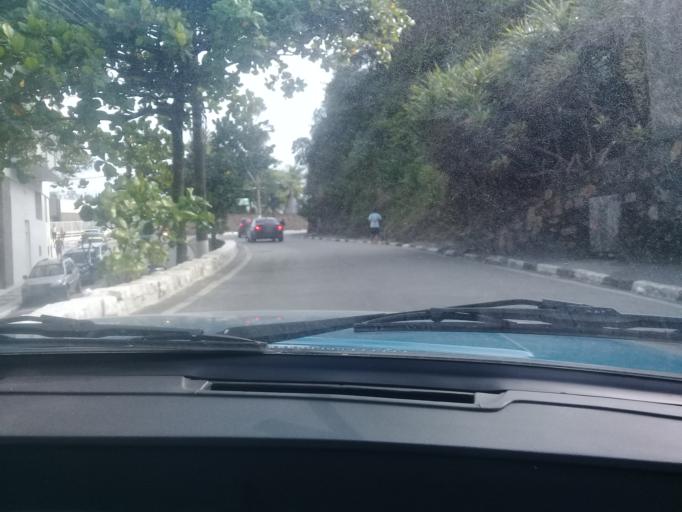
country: BR
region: Sao Paulo
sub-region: Guaruja
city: Guaruja
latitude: -24.0050
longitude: -46.2597
